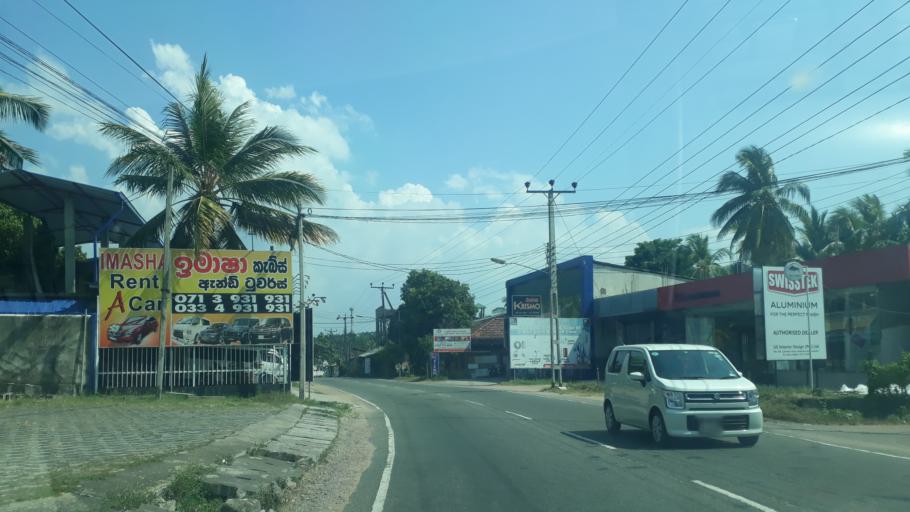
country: LK
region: Western
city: Gampaha
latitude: 7.0847
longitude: 80.0093
